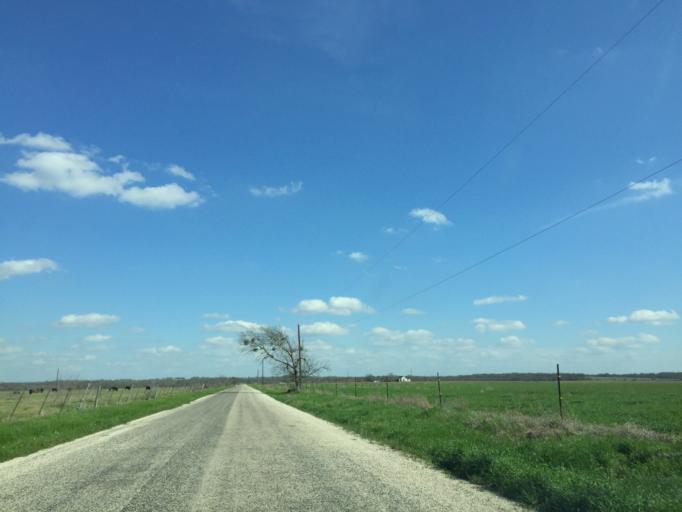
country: US
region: Texas
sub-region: Milam County
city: Thorndale
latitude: 30.5982
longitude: -97.1743
